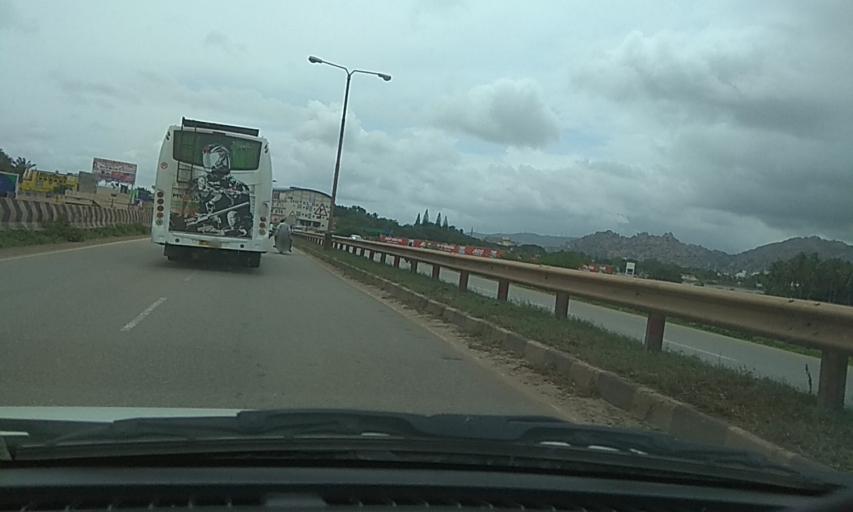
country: IN
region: Karnataka
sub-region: Chitradurga
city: Chitradurga
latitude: 14.2372
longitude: 76.3818
